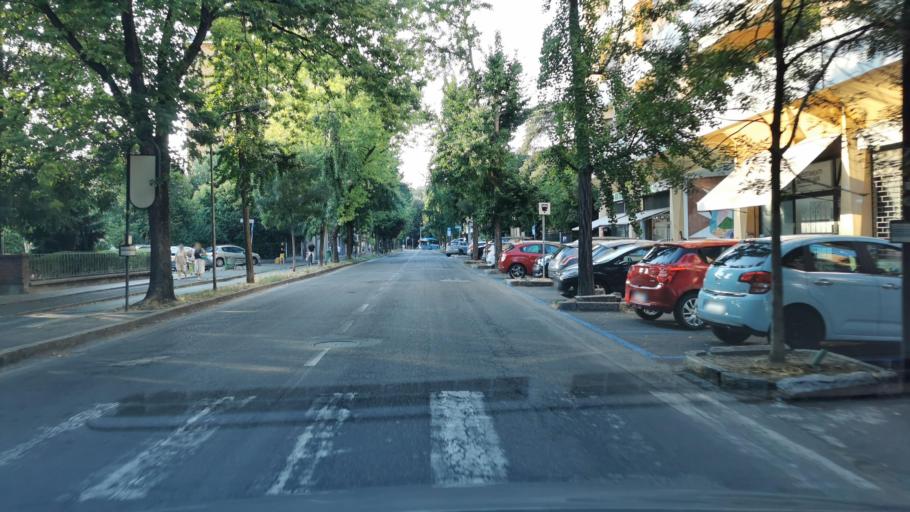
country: IT
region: Emilia-Romagna
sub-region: Provincia di Modena
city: Modena
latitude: 44.6384
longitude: 10.9296
